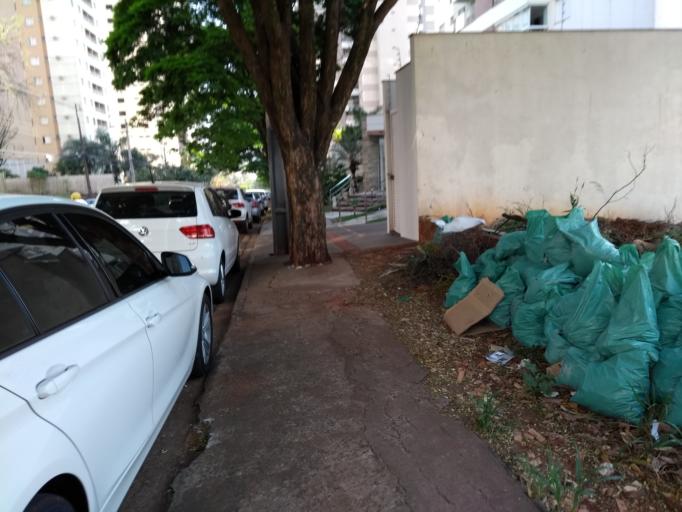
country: BR
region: Parana
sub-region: Londrina
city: Londrina
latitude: -23.3321
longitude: -51.1744
